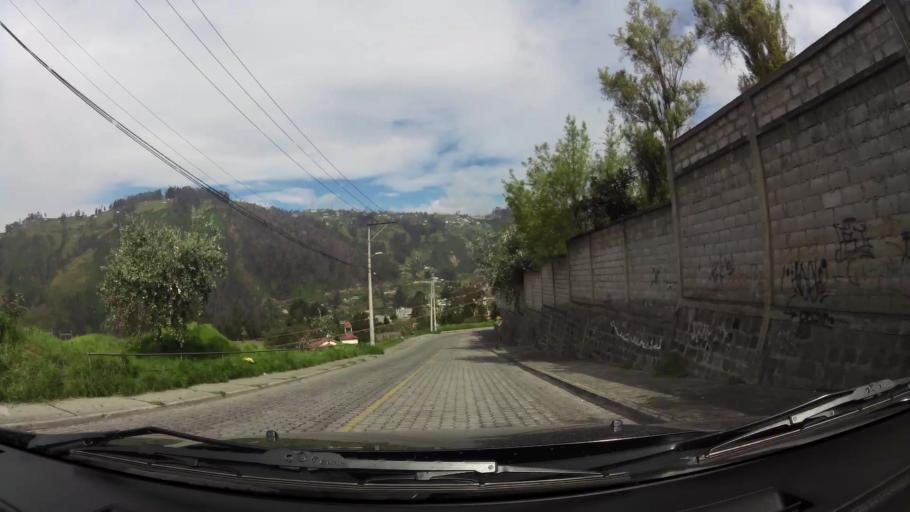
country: EC
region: Pichincha
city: Quito
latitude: -0.2158
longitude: -78.4853
